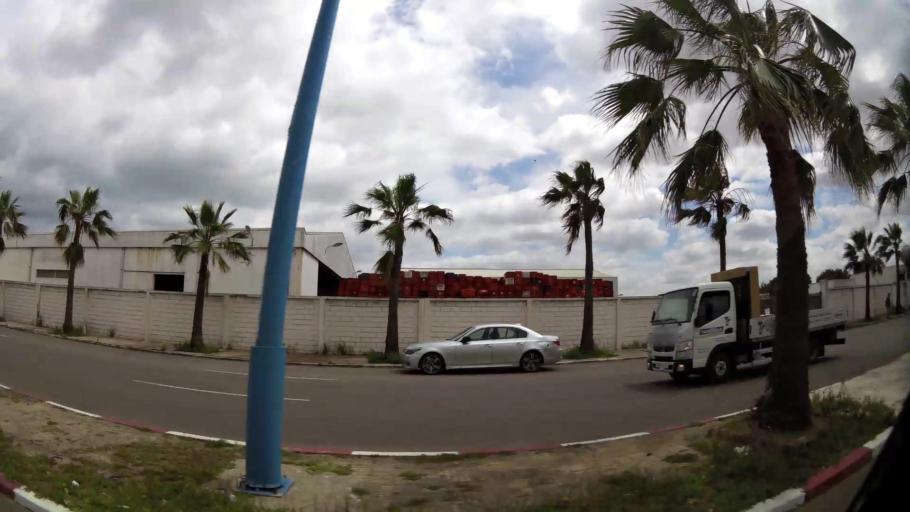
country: MA
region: Grand Casablanca
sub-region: Casablanca
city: Casablanca
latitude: 33.6137
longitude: -7.5512
